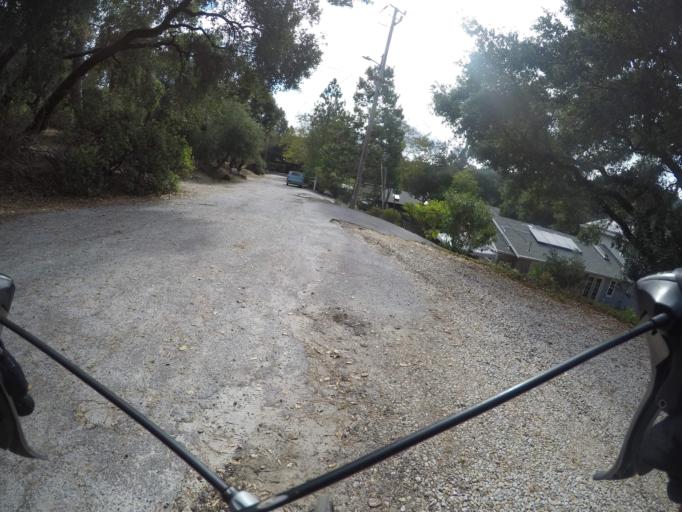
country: US
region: California
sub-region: Santa Cruz County
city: Ben Lomond
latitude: 37.0883
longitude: -122.0822
